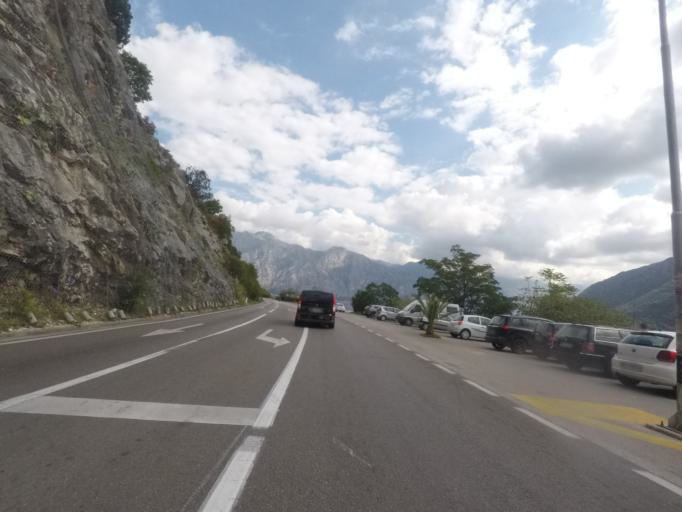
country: ME
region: Kotor
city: Risan
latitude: 42.4842
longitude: 18.7079
